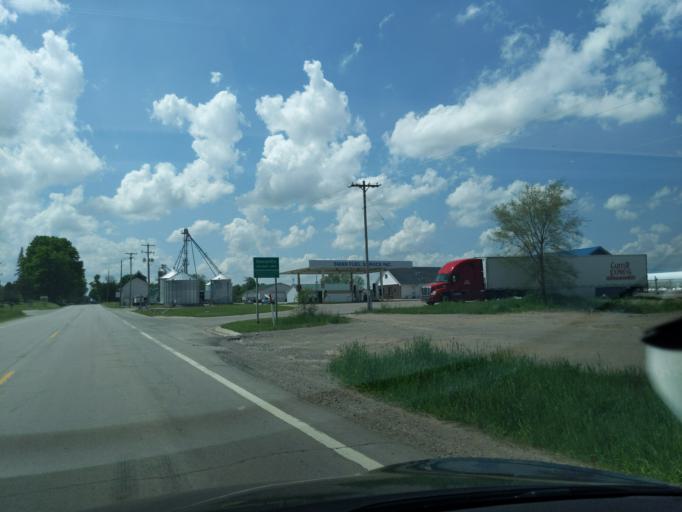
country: US
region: Michigan
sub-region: Ingham County
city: Williamston
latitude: 42.5559
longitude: -84.2927
